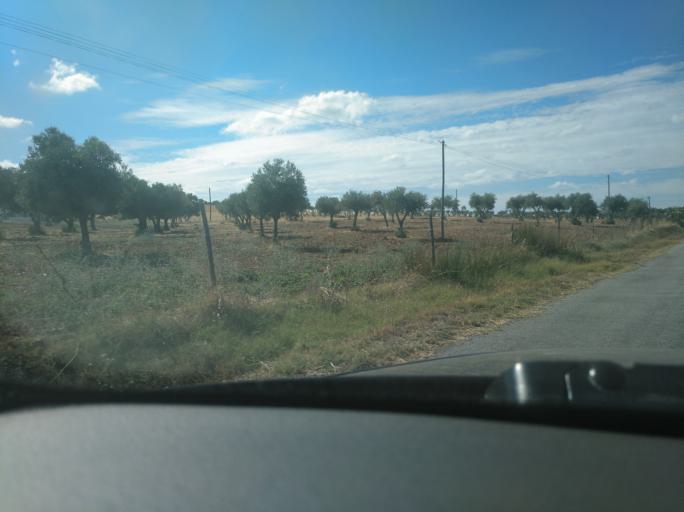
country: ES
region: Extremadura
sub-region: Provincia de Badajoz
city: La Codosera
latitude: 39.1507
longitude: -7.1592
